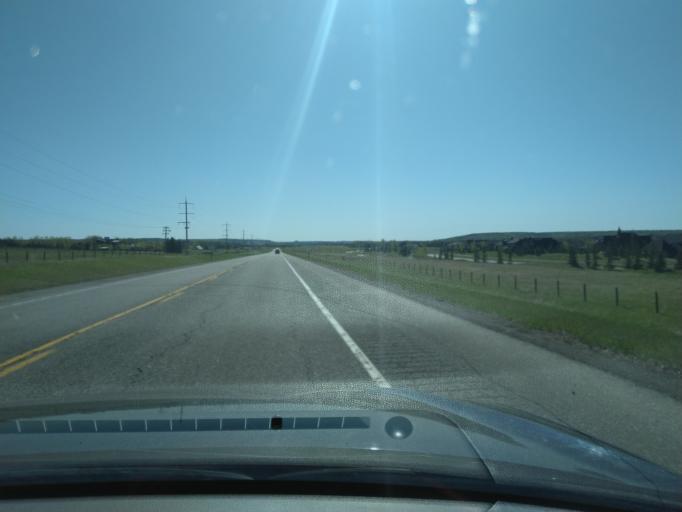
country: CA
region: Alberta
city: Cochrane
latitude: 51.0196
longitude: -114.3178
